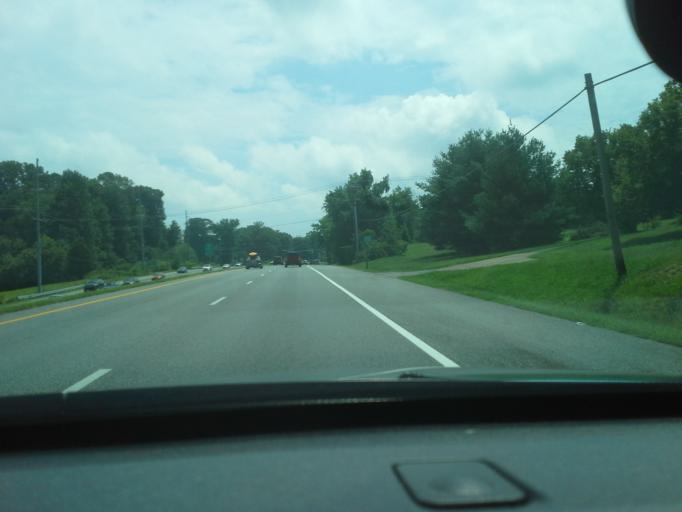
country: US
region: Maryland
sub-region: Calvert County
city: Huntingtown Town Center
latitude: 38.6646
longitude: -76.6111
